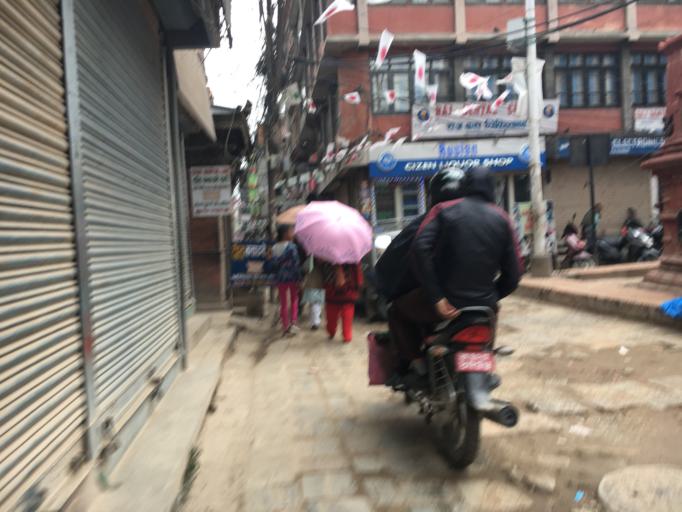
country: NP
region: Central Region
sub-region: Bagmati Zone
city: Kathmandu
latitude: 27.7082
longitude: 85.3103
